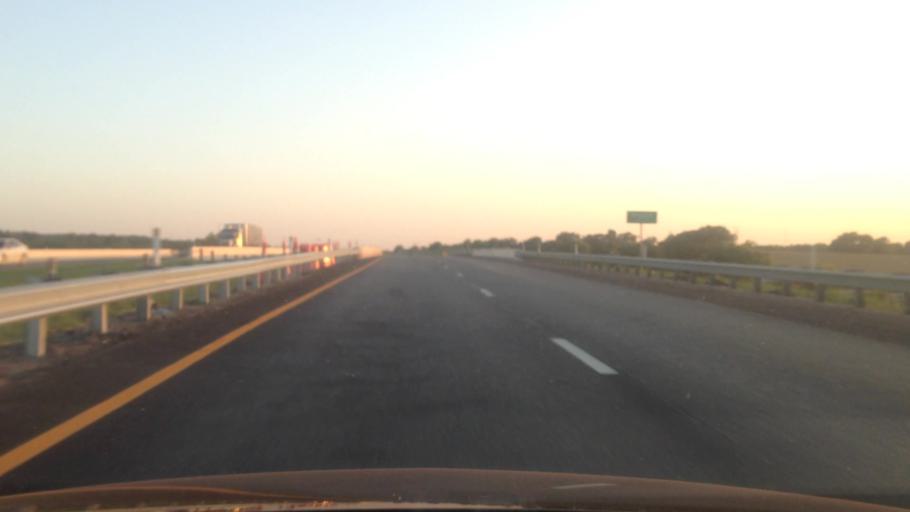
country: US
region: Texas
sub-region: Denton County
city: Argyle
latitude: 33.1318
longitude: -97.2068
